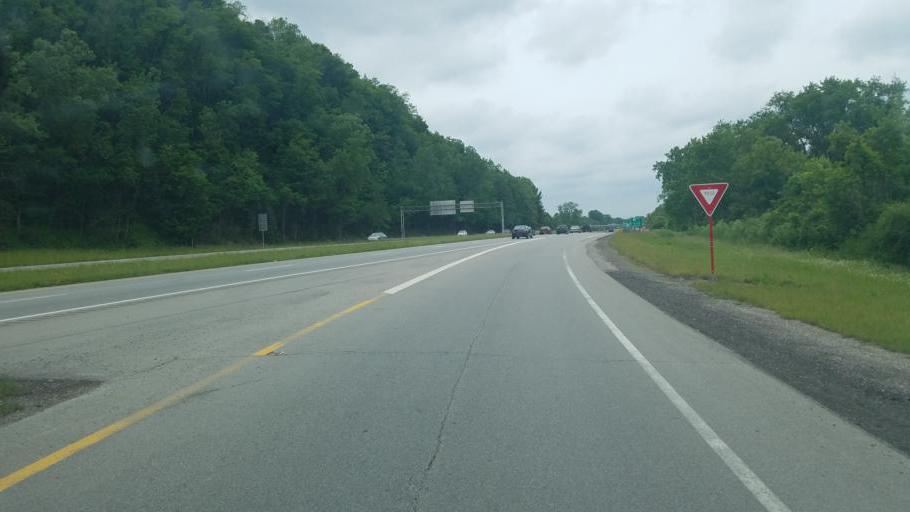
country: US
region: Ohio
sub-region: Licking County
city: Granville
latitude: 40.0595
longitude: -82.5223
